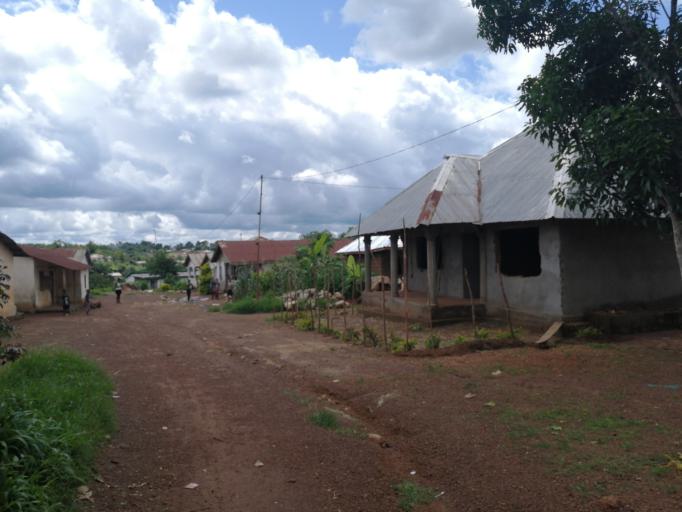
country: SL
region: Northern Province
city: Port Loko
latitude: 8.7723
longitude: -12.7785
